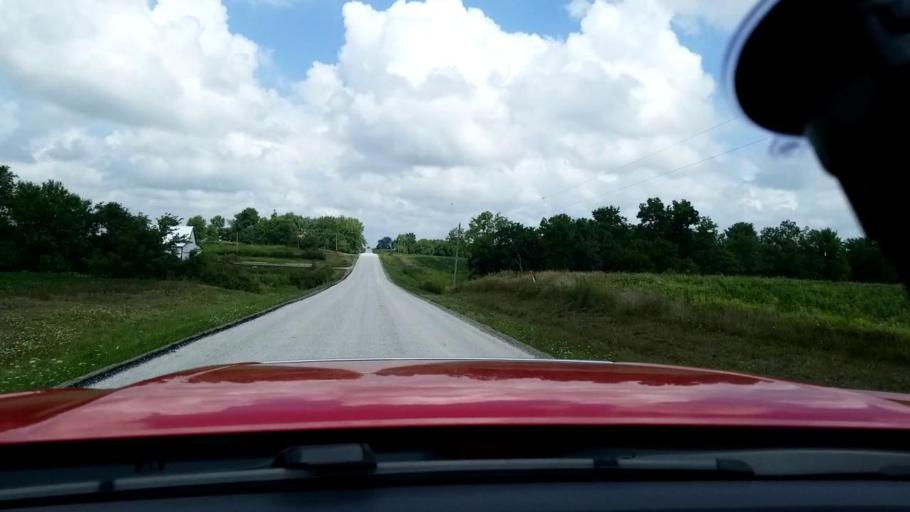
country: US
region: Iowa
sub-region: Decatur County
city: Lamoni
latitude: 40.6307
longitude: -94.0533
